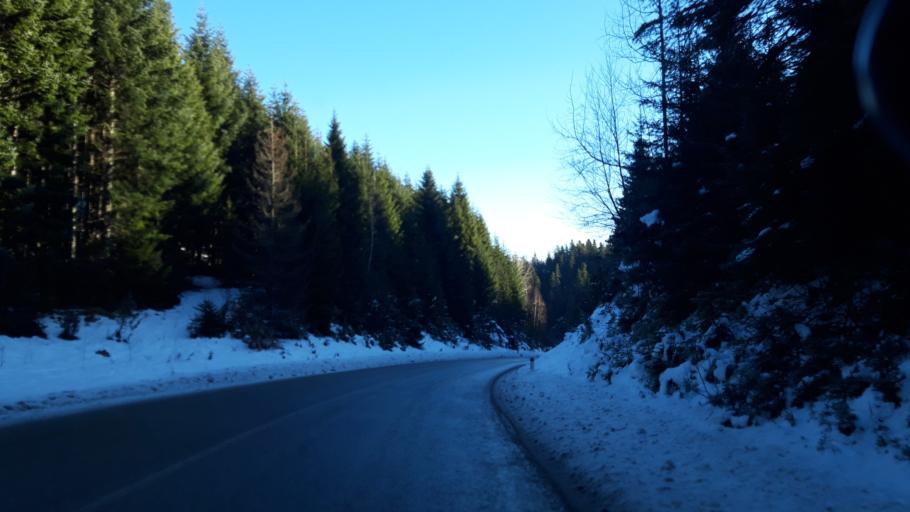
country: BA
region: Republika Srpska
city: Koran
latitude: 43.7886
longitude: 18.5536
